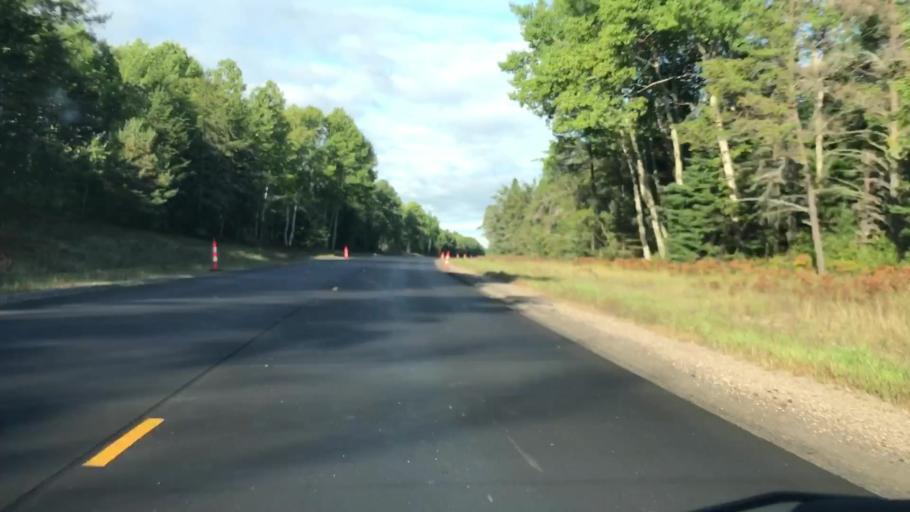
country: US
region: Michigan
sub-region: Mackinac County
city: Saint Ignace
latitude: 46.3460
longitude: -84.9235
